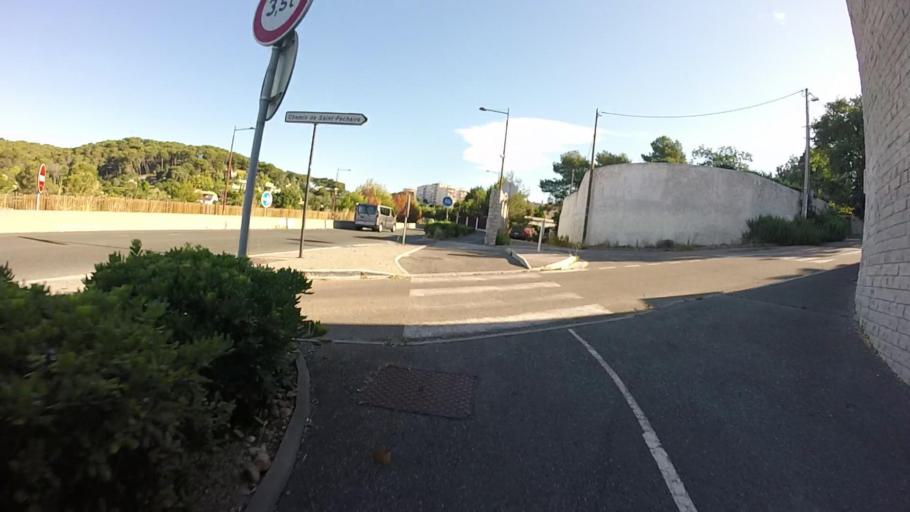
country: FR
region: Provence-Alpes-Cote d'Azur
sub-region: Departement des Alpes-Maritimes
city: Biot
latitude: 43.5893
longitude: 7.0922
